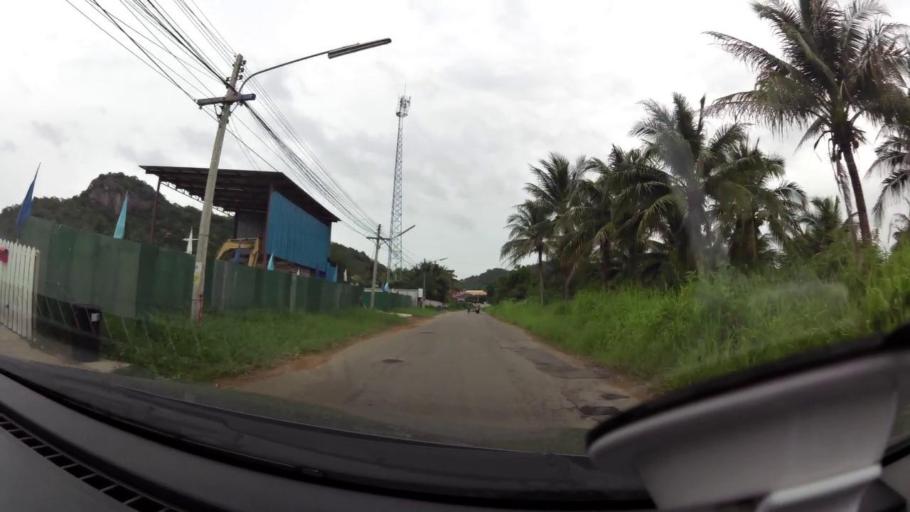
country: TH
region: Prachuap Khiri Khan
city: Pran Buri
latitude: 12.4478
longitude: 99.9712
